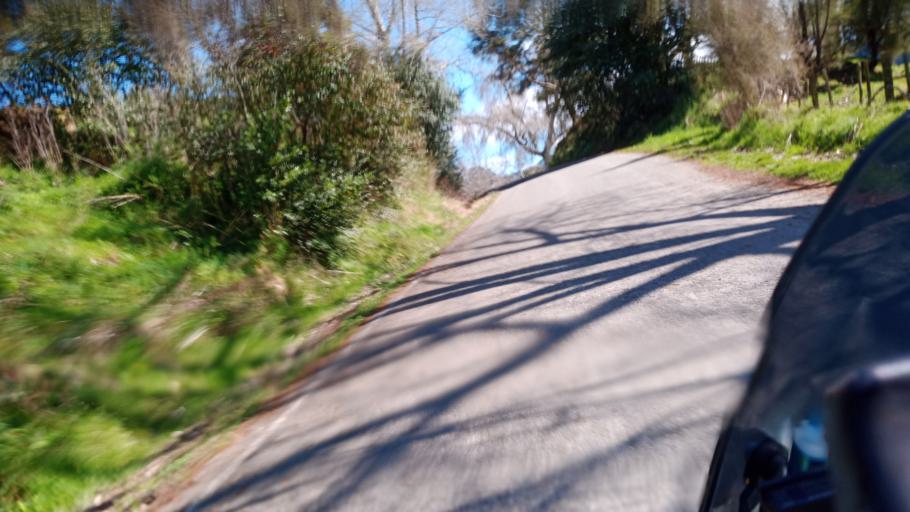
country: NZ
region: Gisborne
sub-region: Gisborne District
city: Gisborne
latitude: -38.7872
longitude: 177.7852
